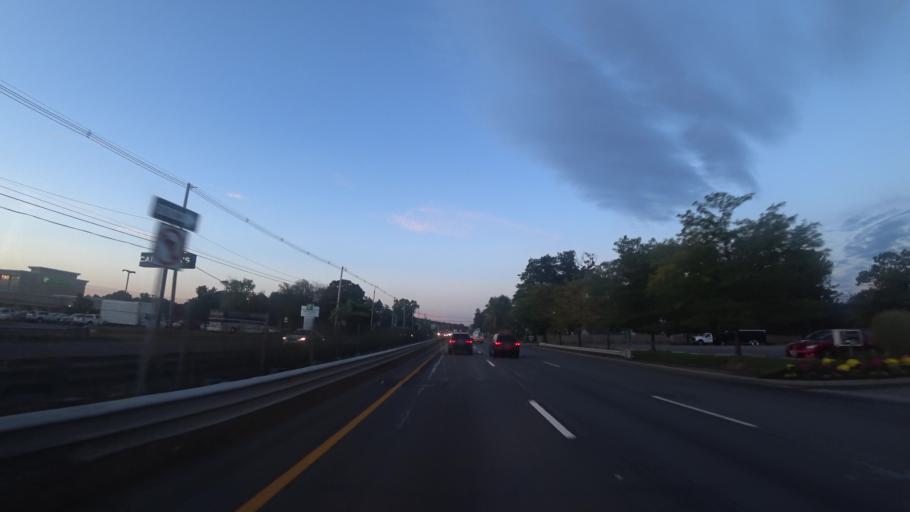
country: US
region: Massachusetts
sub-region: Essex County
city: South Peabody
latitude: 42.5206
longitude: -70.9984
